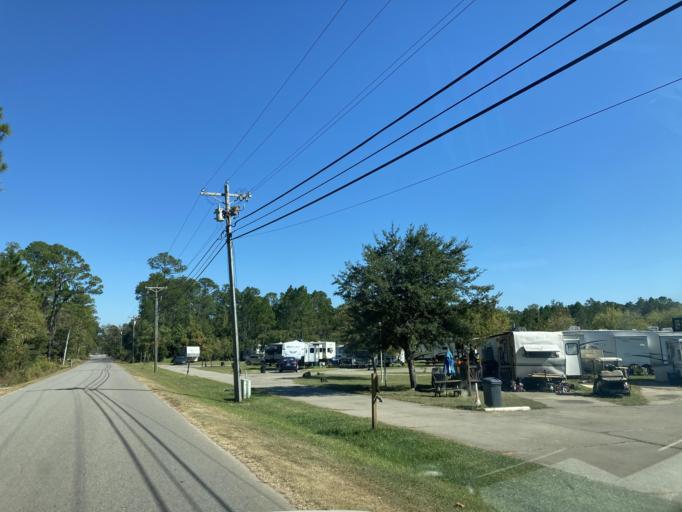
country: US
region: Mississippi
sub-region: Jackson County
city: Saint Martin
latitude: 30.4649
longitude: -88.8522
